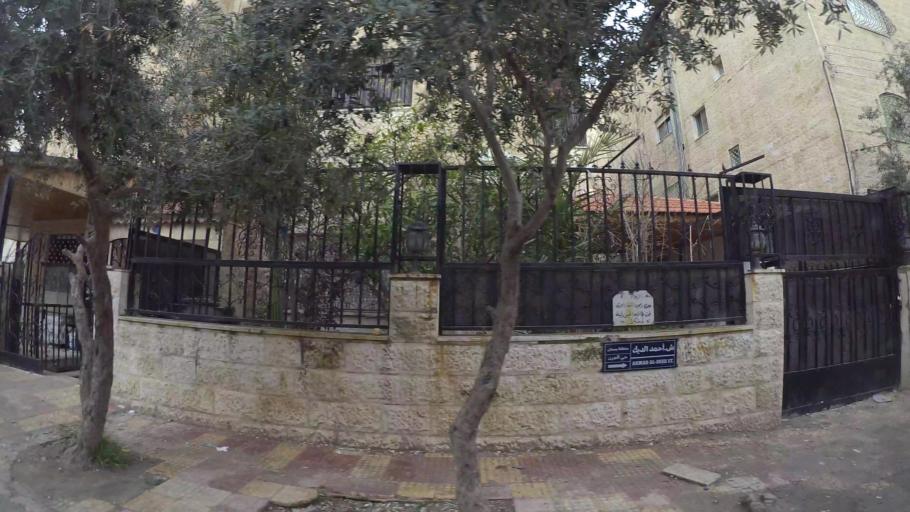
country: JO
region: Amman
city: Amman
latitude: 31.9868
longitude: 35.9249
